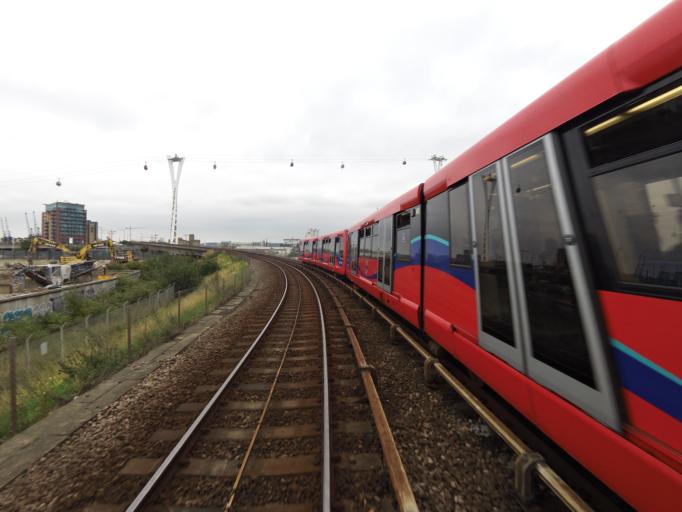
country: GB
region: England
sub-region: Greater London
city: Poplar
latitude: 51.5066
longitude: 0.0128
